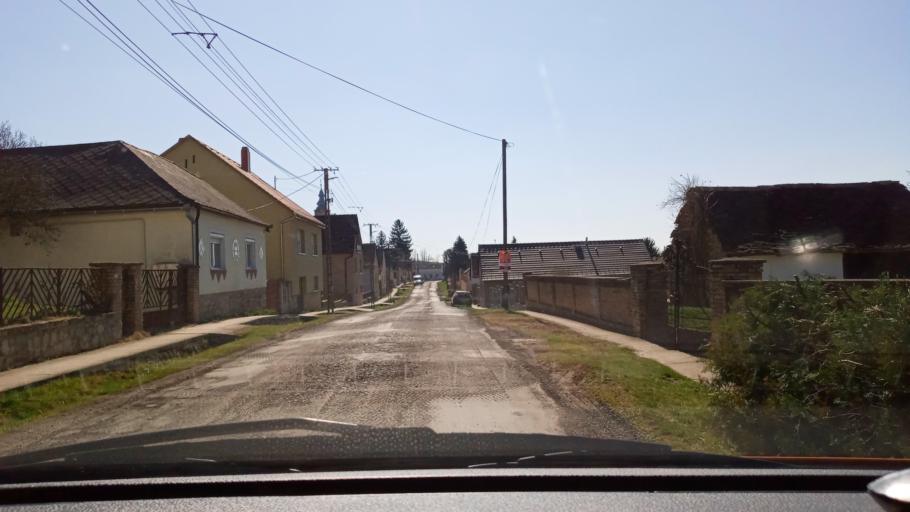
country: HU
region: Baranya
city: Boly
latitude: 46.0100
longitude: 18.4146
